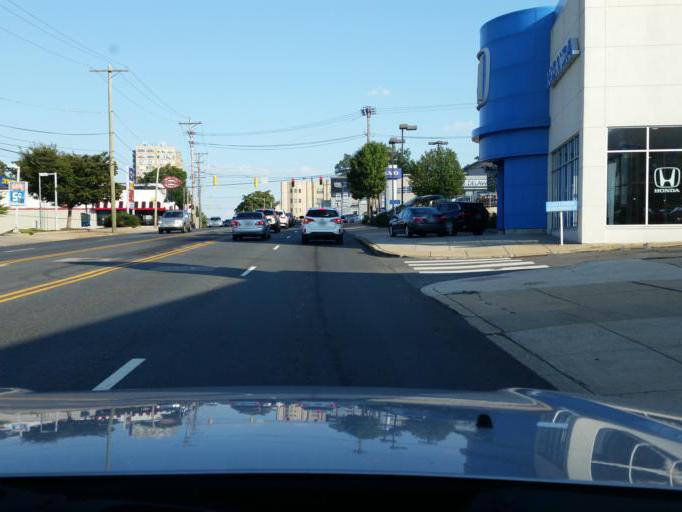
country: US
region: Delaware
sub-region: New Castle County
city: Wilmington
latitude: 39.7550
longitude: -75.5657
